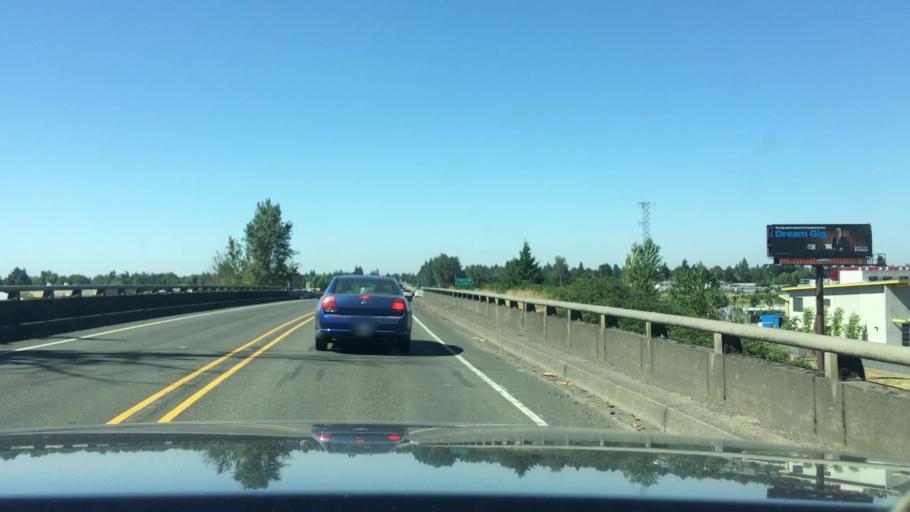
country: US
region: Oregon
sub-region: Lane County
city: Eugene
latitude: 44.0598
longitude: -123.1736
